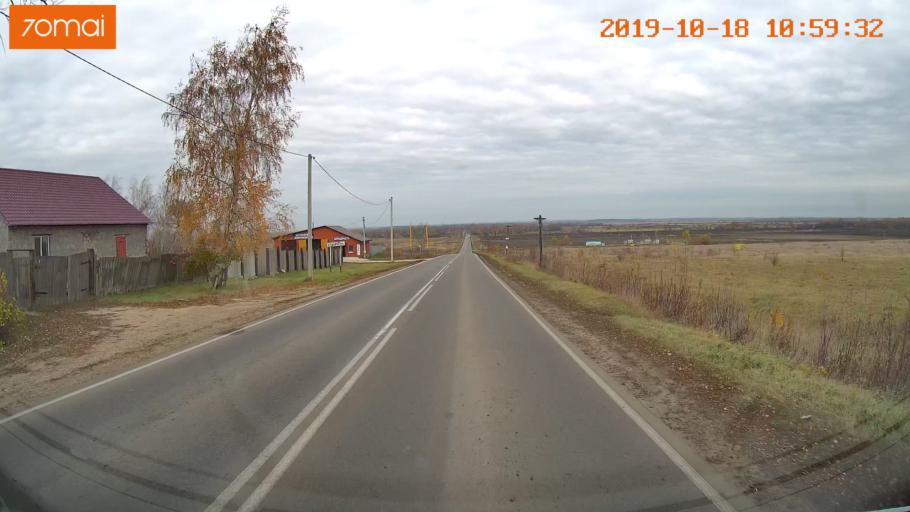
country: RU
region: Tula
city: Yepifan'
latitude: 53.8309
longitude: 38.5570
